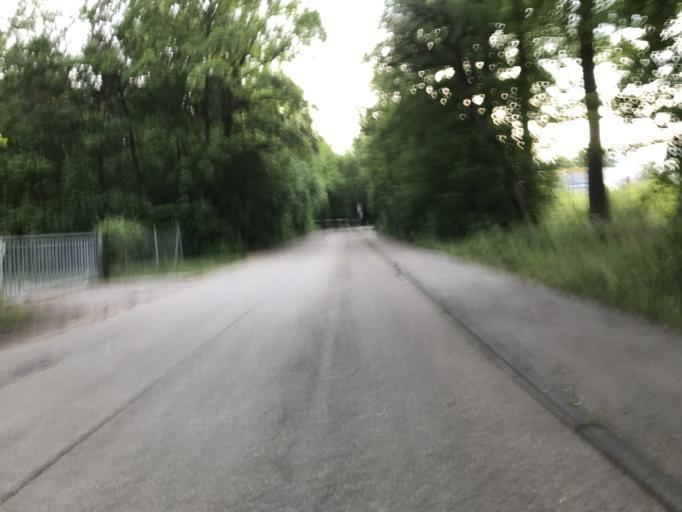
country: DE
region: Baden-Wuerttemberg
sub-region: Regierungsbezirk Stuttgart
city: Stuttgart Feuerbach
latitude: 48.8294
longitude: 9.1504
